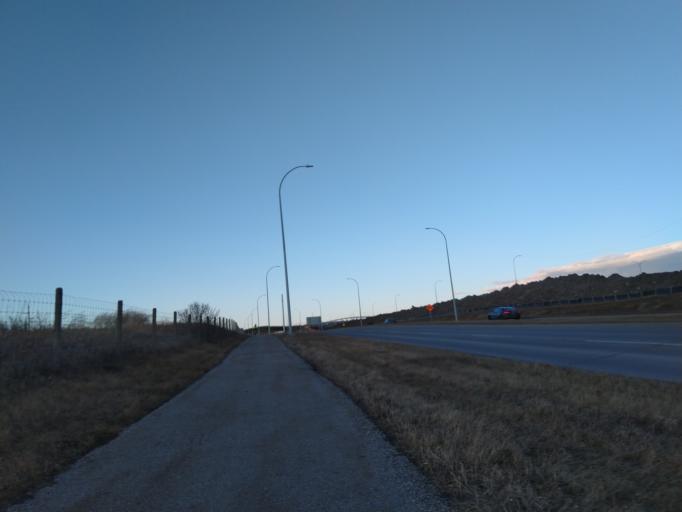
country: CA
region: Alberta
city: Calgary
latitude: 51.1205
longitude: -114.2331
